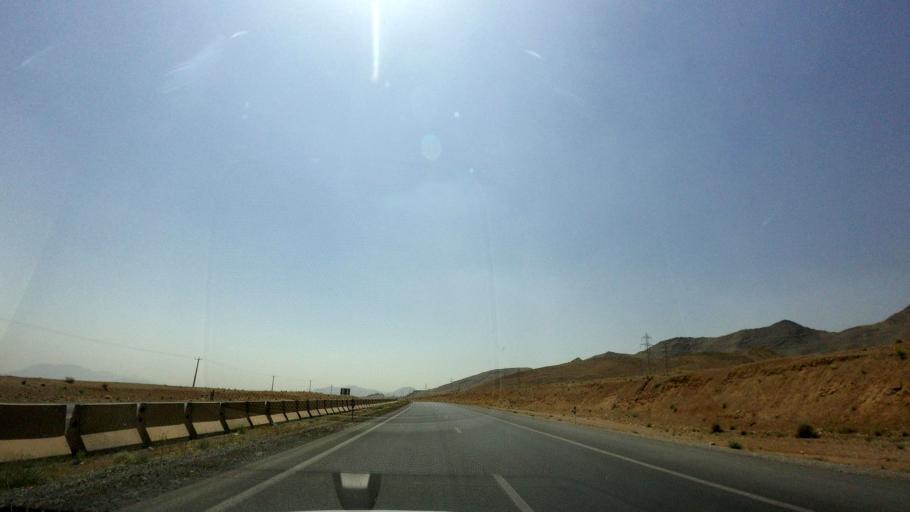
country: IR
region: Isfahan
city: Najafabad
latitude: 32.5439
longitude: 51.3121
